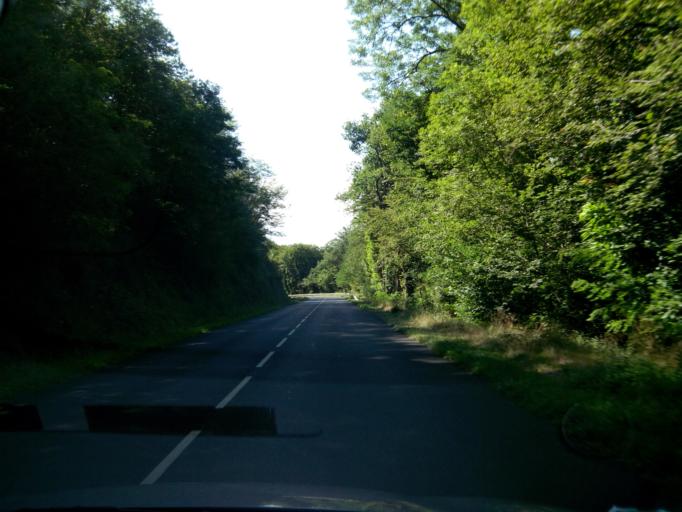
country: FR
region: Limousin
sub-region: Departement de la Correze
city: Beynat
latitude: 45.1227
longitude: 1.6969
